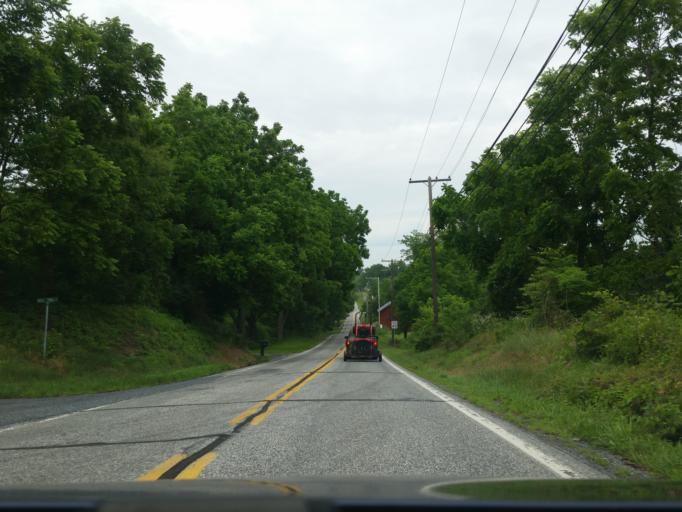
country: US
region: Pennsylvania
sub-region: Lebanon County
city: Palmyra
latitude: 40.3907
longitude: -76.6158
